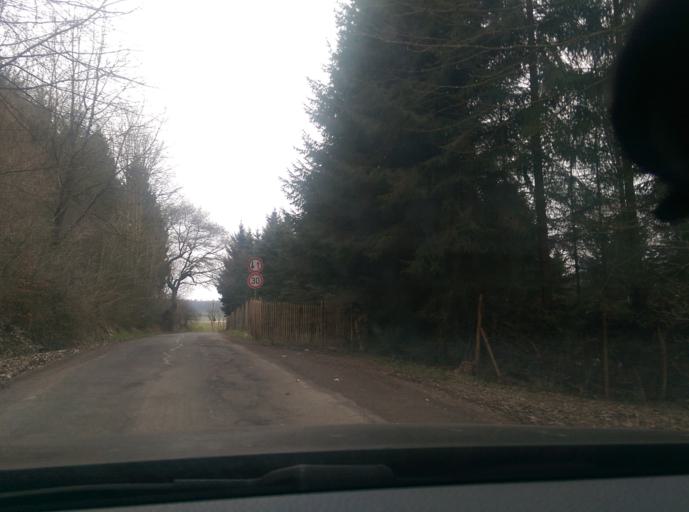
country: DE
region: Lower Saxony
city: Hameln
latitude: 52.1262
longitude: 9.3939
